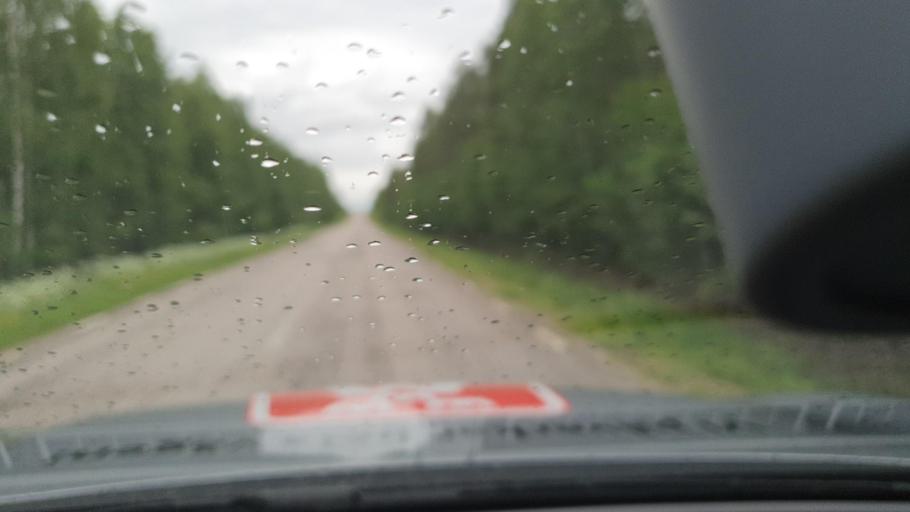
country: SE
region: Norrbotten
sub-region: Overkalix Kommun
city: OEverkalix
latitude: 66.3713
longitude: 22.7997
